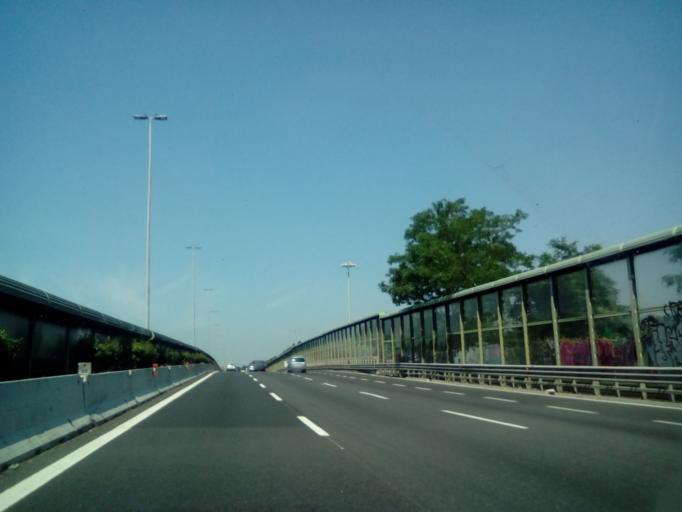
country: IT
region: Latium
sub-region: Citta metropolitana di Roma Capitale
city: Vitinia
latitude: 41.8019
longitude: 12.4463
